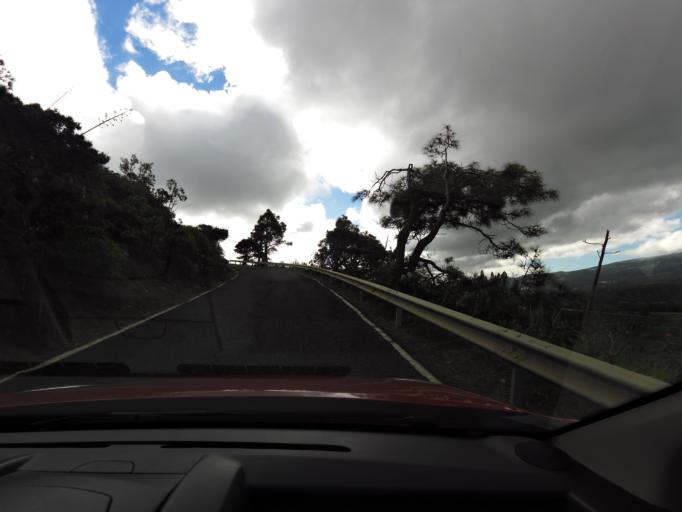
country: ES
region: Canary Islands
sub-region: Provincia de Las Palmas
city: Santa Brigida
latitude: 28.0375
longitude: -15.4593
